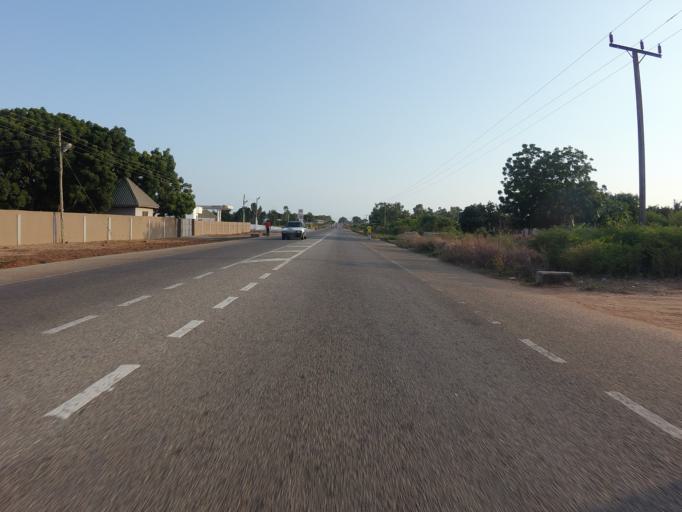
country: GH
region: Volta
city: Anloga
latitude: 6.0161
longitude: 0.5987
